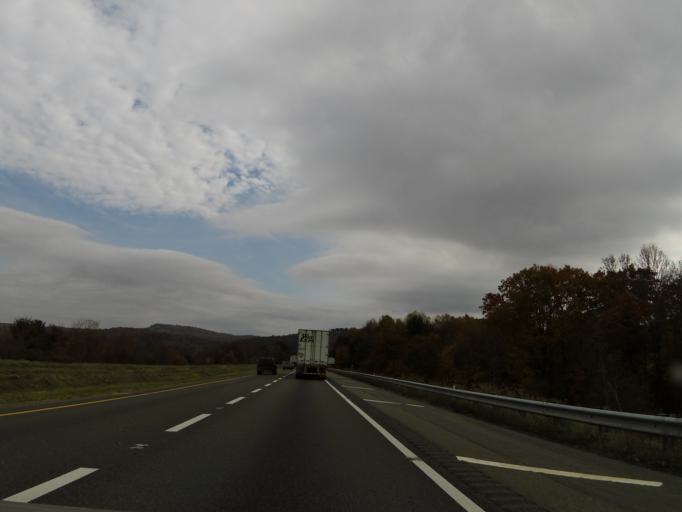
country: US
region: Virginia
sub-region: Carroll County
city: Hillsville
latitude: 36.6820
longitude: -80.7170
